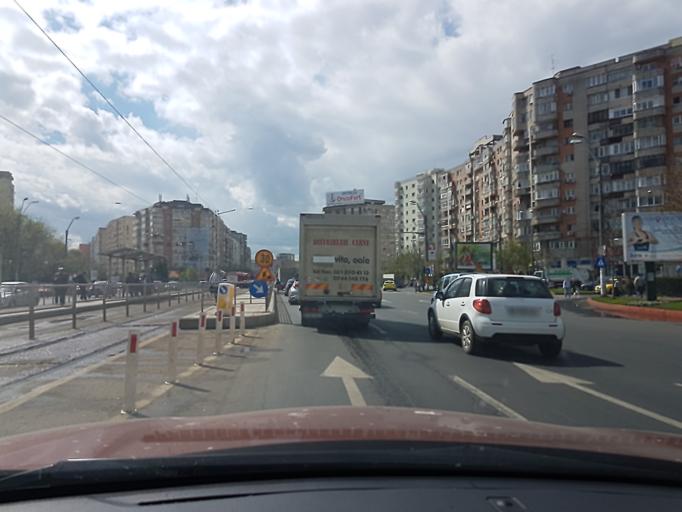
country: RO
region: Bucuresti
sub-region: Municipiul Bucuresti
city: Bucharest
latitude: 44.4254
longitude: 26.1374
